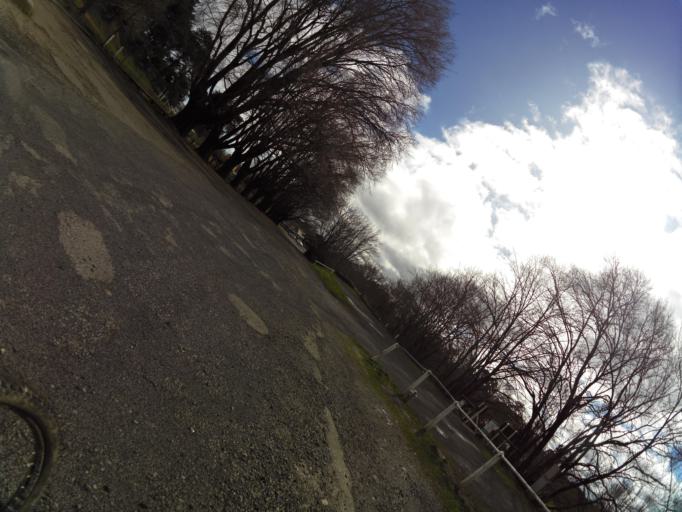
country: AU
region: Victoria
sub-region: Mount Alexander
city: Castlemaine
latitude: -37.3415
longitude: 144.1534
